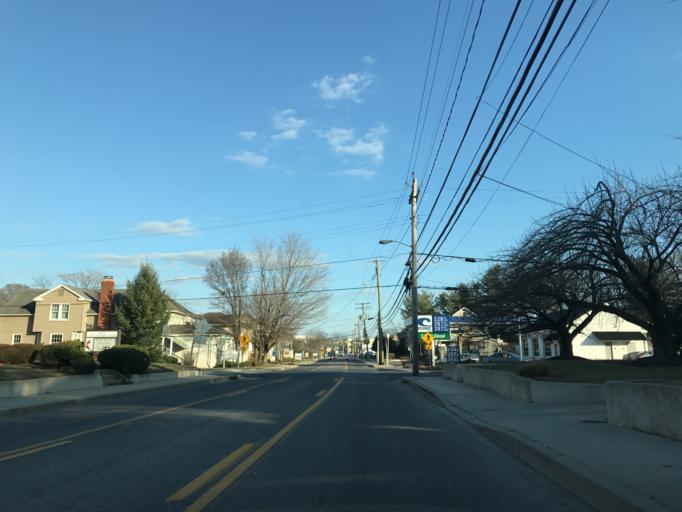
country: US
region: Maryland
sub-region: Anne Arundel County
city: Parole
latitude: 38.9777
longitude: -76.5142
